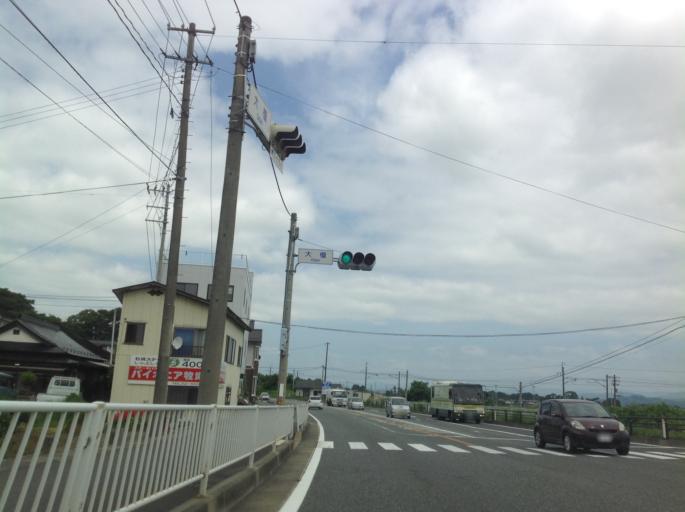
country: JP
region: Iwate
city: Mizusawa
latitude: 39.1158
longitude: 141.1457
